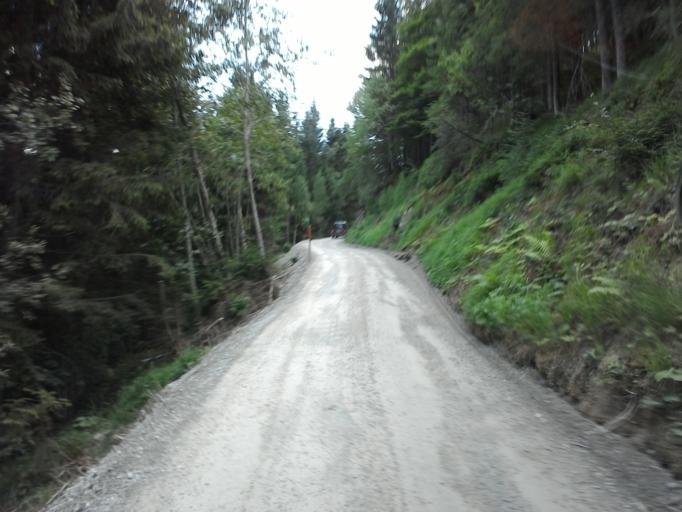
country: AT
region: Tyrol
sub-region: Politischer Bezirk Lienz
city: Untertilliach
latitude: 46.7000
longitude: 12.7640
